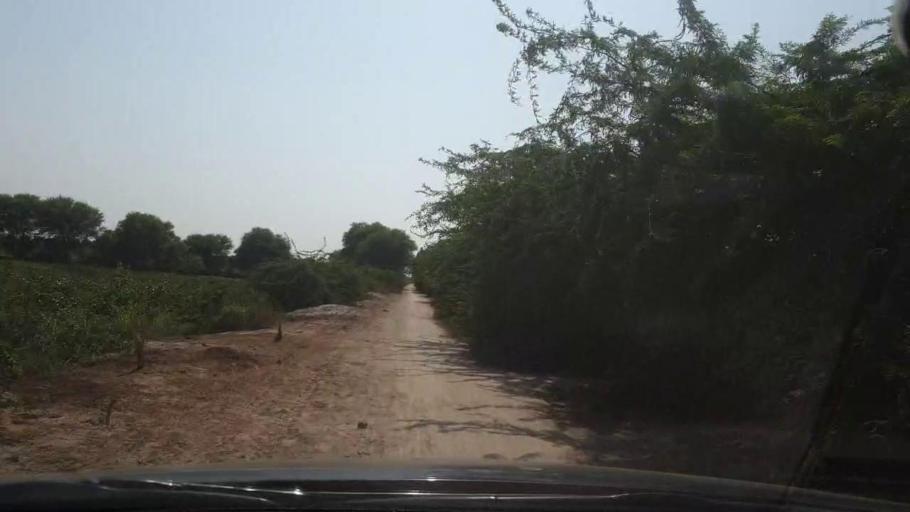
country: PK
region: Sindh
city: Naukot
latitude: 24.8056
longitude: 69.2571
